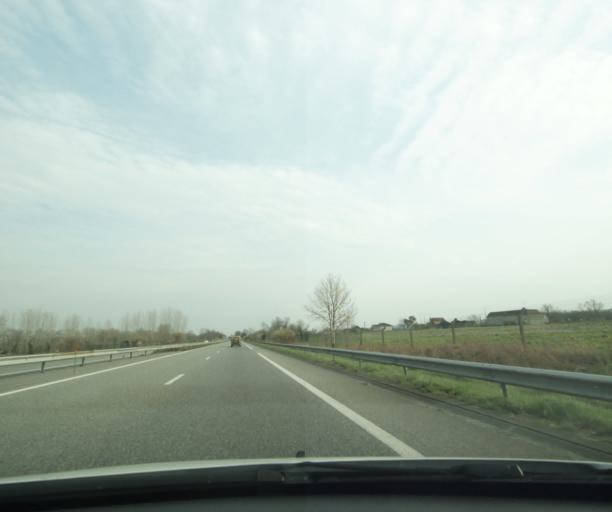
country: FR
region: Aquitaine
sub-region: Departement des Pyrenees-Atlantiques
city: Orthez
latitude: 43.4636
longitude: -0.7297
